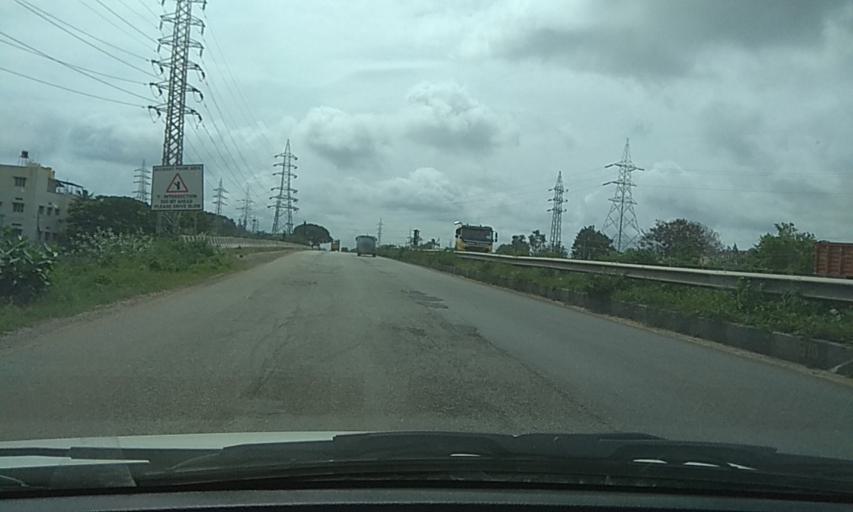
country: IN
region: Karnataka
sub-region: Davanagere
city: Harihar
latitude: 14.4324
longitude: 75.9200
